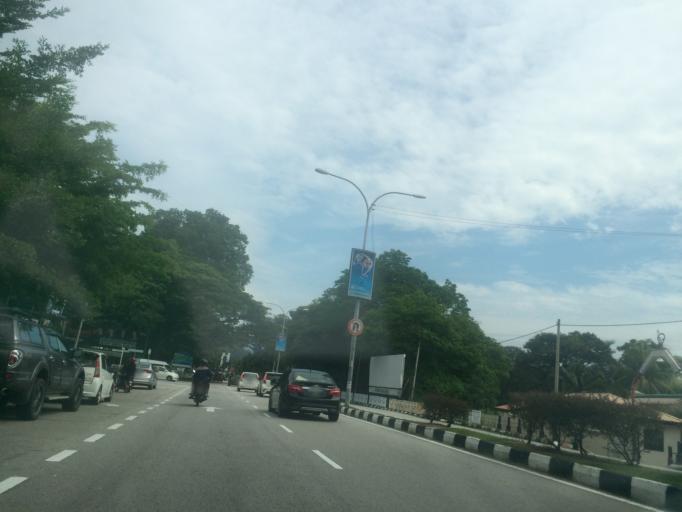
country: MY
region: Perak
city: Ipoh
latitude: 4.6035
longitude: 101.0945
